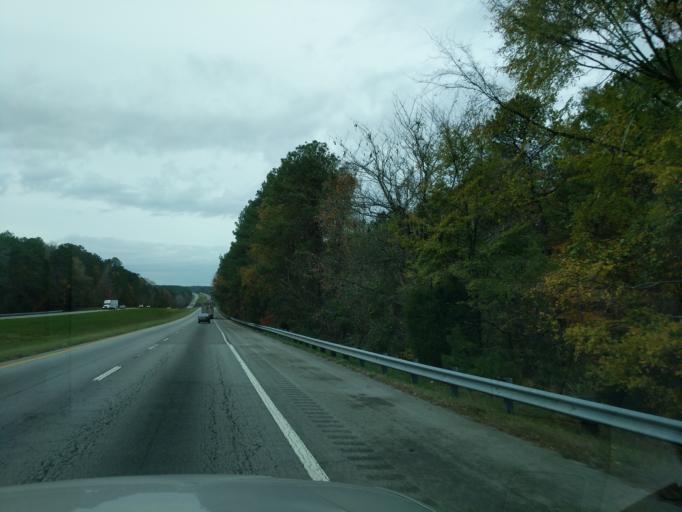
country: US
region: South Carolina
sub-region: Newberry County
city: Newberry
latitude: 34.3846
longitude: -81.6847
